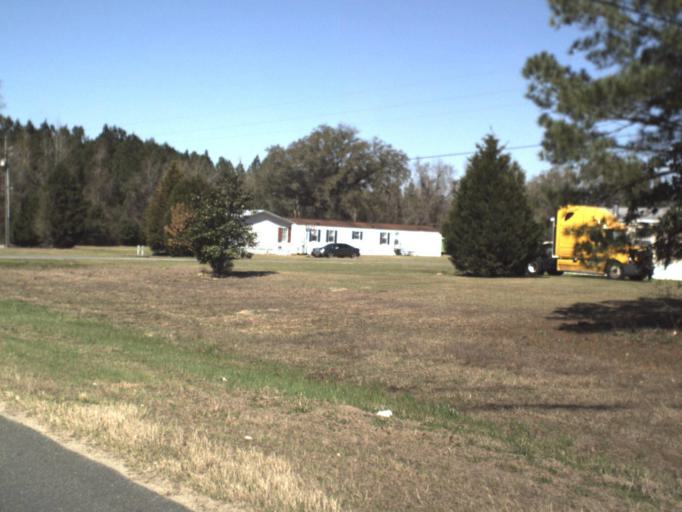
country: US
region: Florida
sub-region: Jackson County
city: Marianna
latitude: 30.7453
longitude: -85.1657
